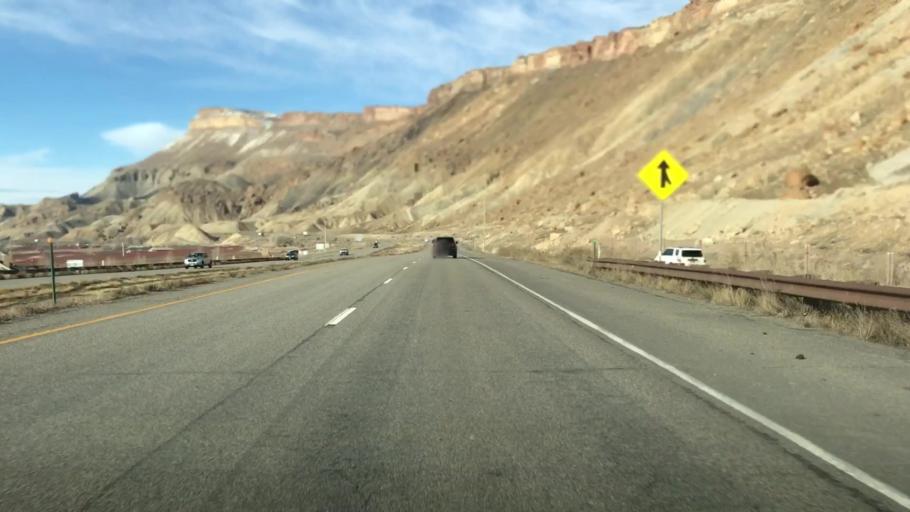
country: US
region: Colorado
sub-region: Mesa County
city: Palisade
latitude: 39.1182
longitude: -108.3605
